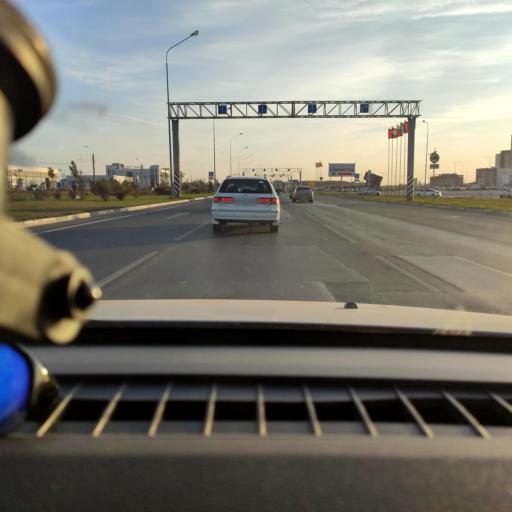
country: RU
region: Samara
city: Samara
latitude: 53.1402
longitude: 50.1779
